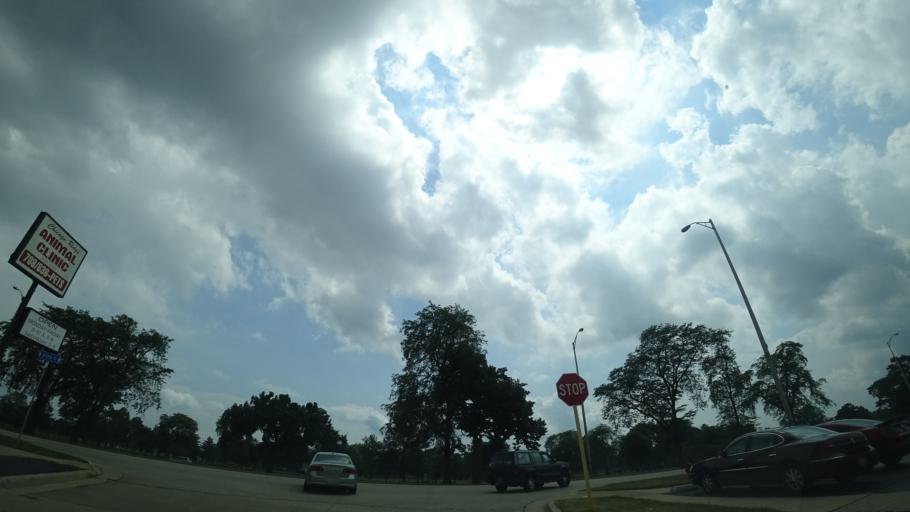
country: US
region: Illinois
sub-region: Cook County
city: Oak Lawn
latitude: 41.6907
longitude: -87.7617
